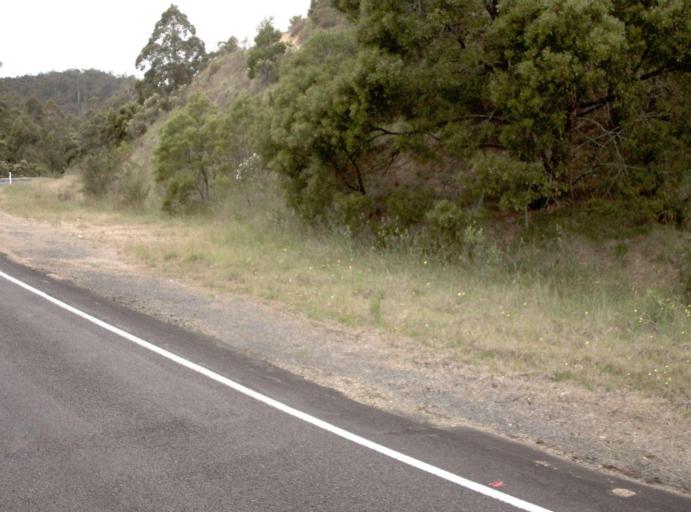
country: AU
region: New South Wales
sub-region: Bombala
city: Bombala
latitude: -37.2444
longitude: 149.2589
